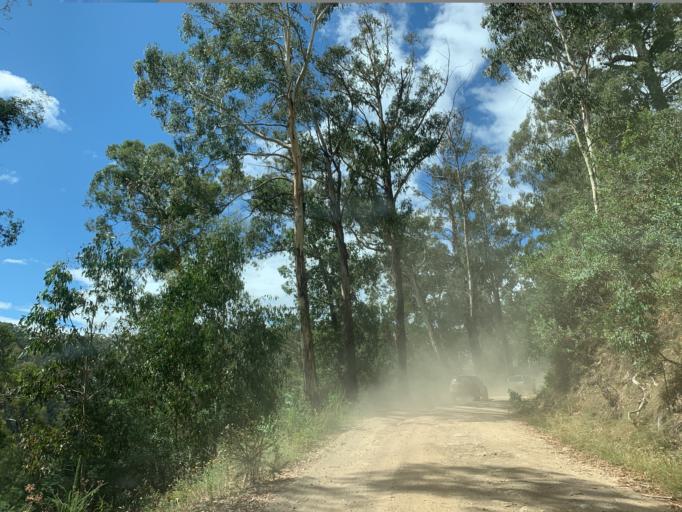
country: AU
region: Victoria
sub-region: Mansfield
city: Mansfield
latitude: -37.0925
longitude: 146.5335
